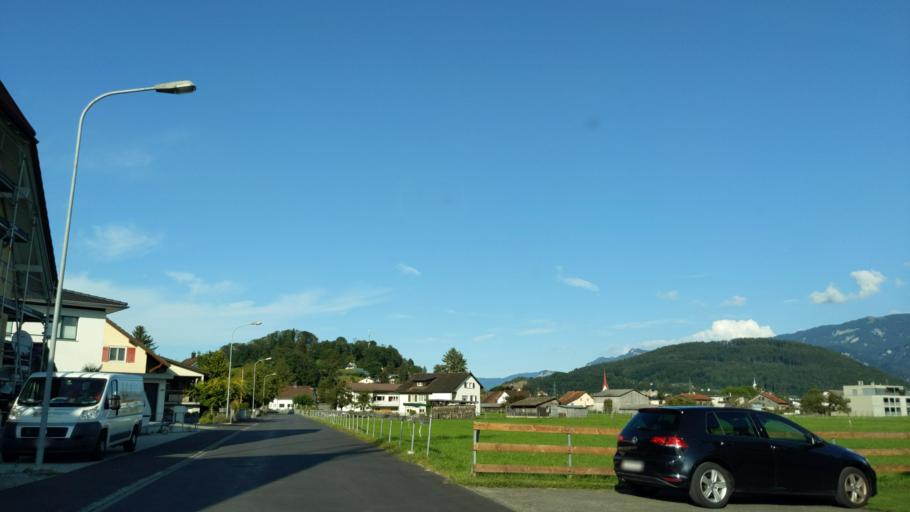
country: AT
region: Vorarlberg
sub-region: Politischer Bezirk Feldkirch
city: Koblach
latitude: 47.3319
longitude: 9.5812
